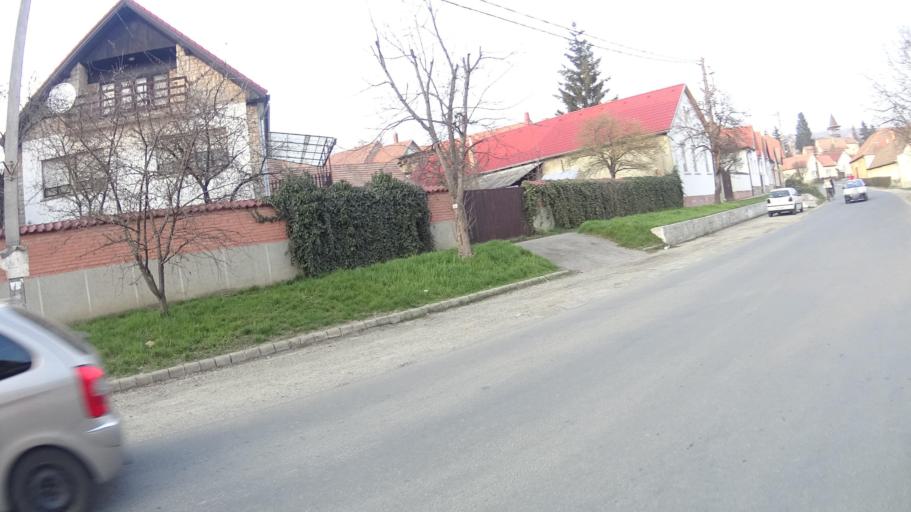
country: HU
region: Pest
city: Veroce
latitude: 47.8251
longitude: 19.0354
